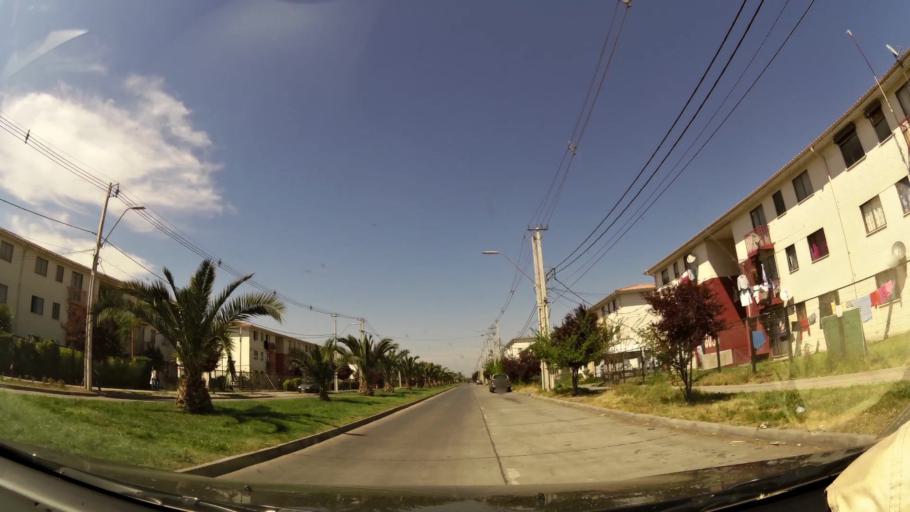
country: CL
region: Santiago Metropolitan
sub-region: Provincia de Santiago
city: Lo Prado
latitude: -33.3929
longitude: -70.7521
